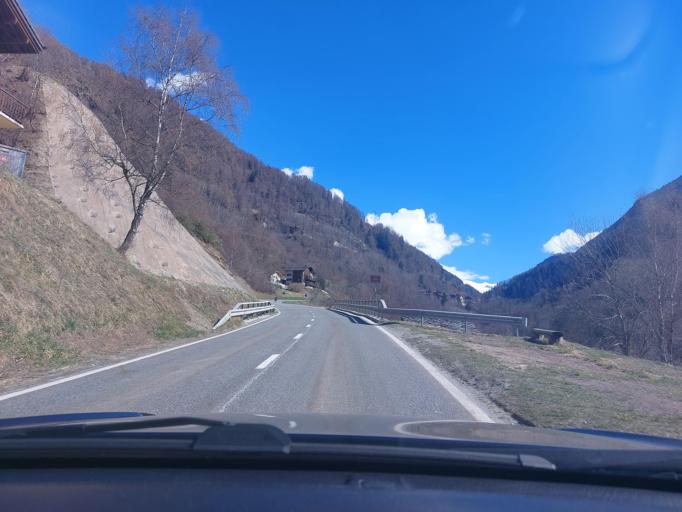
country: CH
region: Valais
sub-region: Herens District
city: Heremence
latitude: 46.1560
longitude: 7.4481
